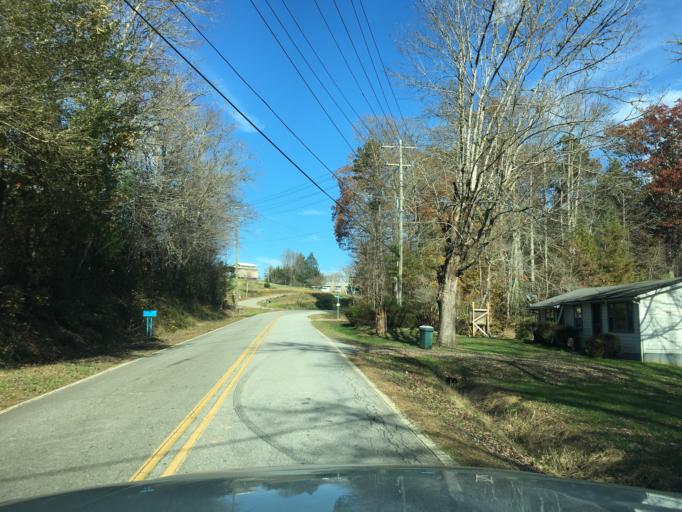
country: US
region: North Carolina
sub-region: Henderson County
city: Etowah
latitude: 35.3132
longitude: -82.6217
